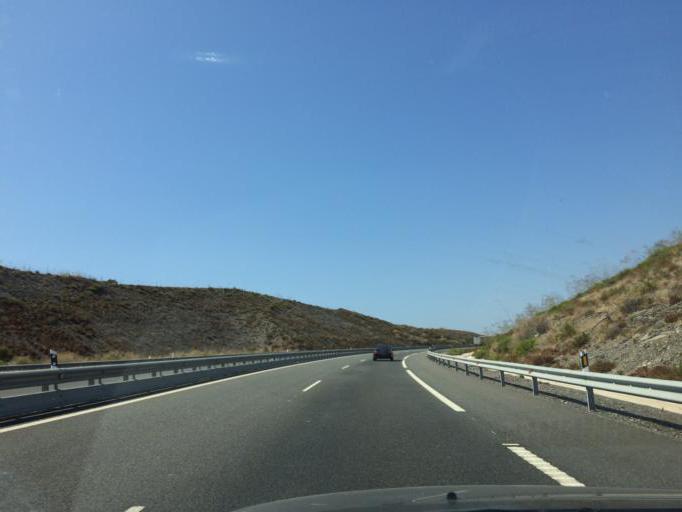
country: ES
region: Andalusia
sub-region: Provincia de Granada
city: Albunol
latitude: 36.7507
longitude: -3.2096
